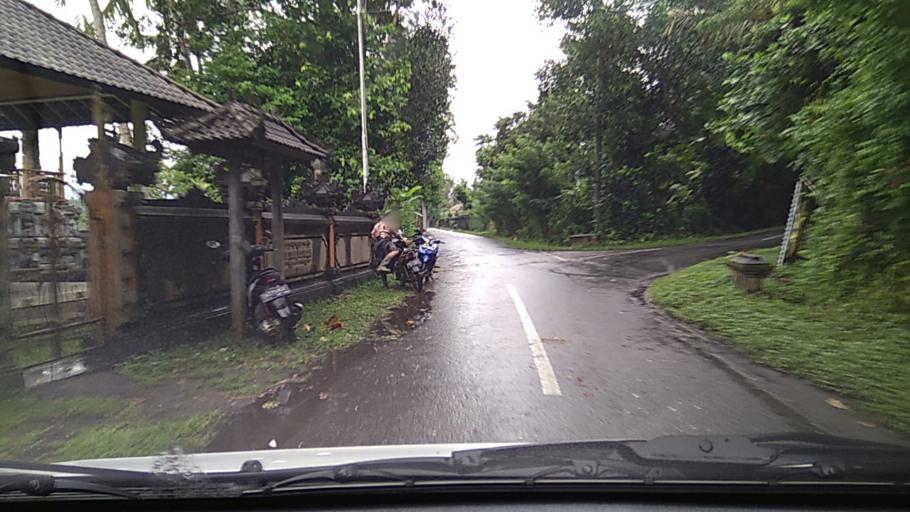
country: ID
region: Bali
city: Tiyingtali Kelod
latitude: -8.3992
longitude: 115.6167
